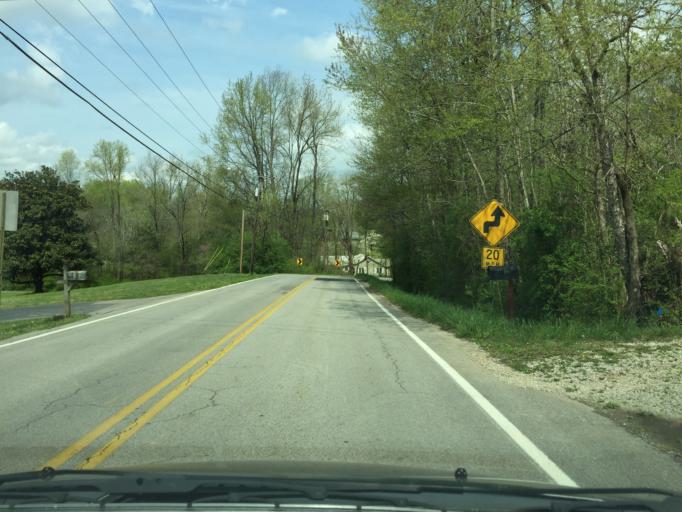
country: US
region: Tennessee
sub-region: Hamilton County
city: Walden
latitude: 35.1560
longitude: -85.2812
